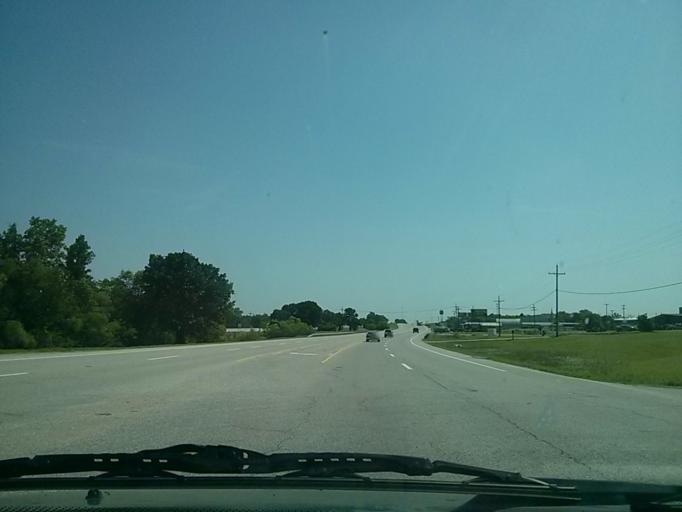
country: US
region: Oklahoma
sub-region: Tulsa County
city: Oakhurst
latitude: 36.0669
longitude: -96.0659
